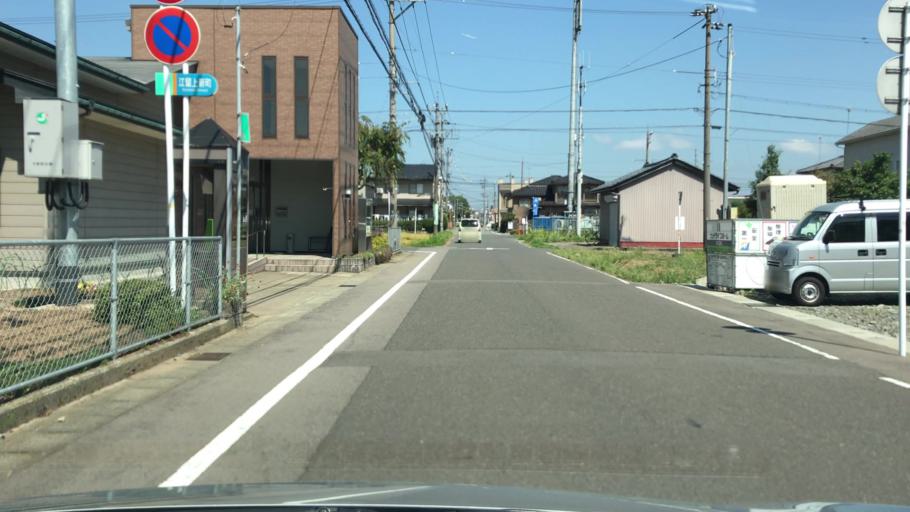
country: JP
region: Fukui
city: Maruoka
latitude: 36.1263
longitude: 136.2176
